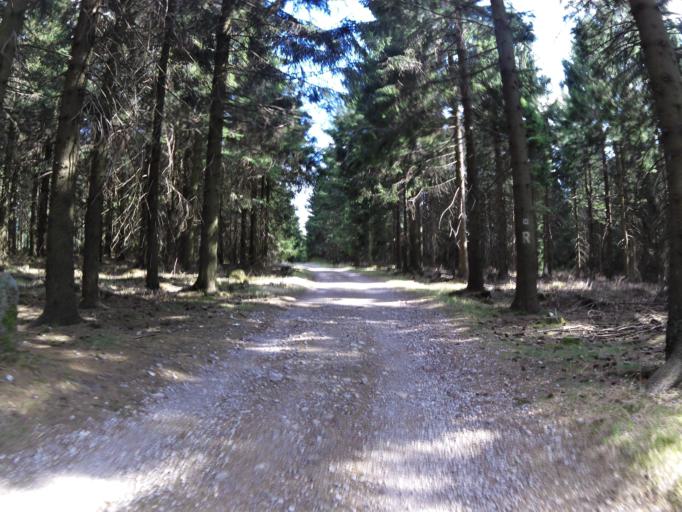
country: DE
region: Thuringia
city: Bermbach
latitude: 50.7198
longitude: 10.6455
